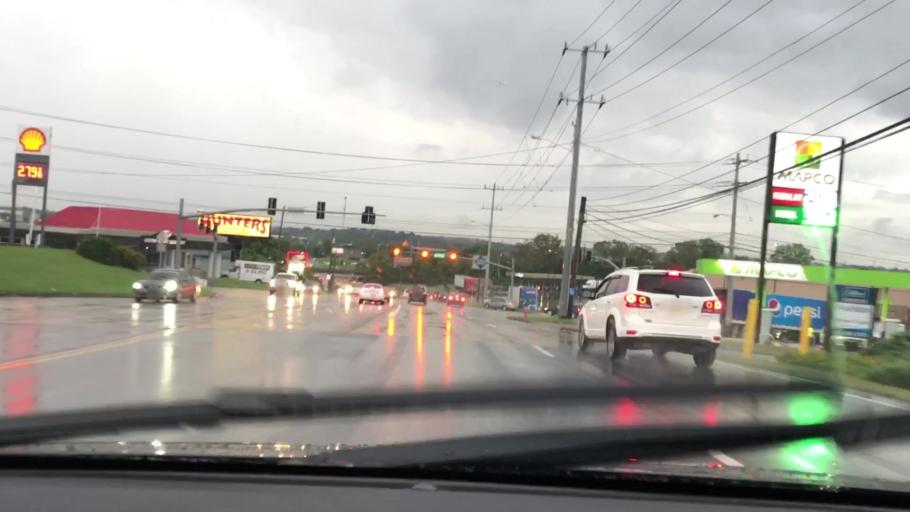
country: US
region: Tennessee
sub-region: Davidson County
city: Oak Hill
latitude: 36.0870
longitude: -86.6931
